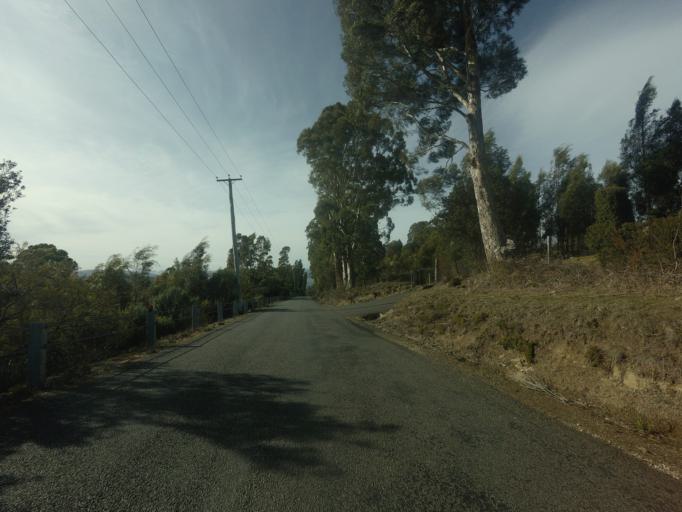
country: AU
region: Tasmania
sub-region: Kingborough
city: Kettering
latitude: -43.1674
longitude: 147.2095
